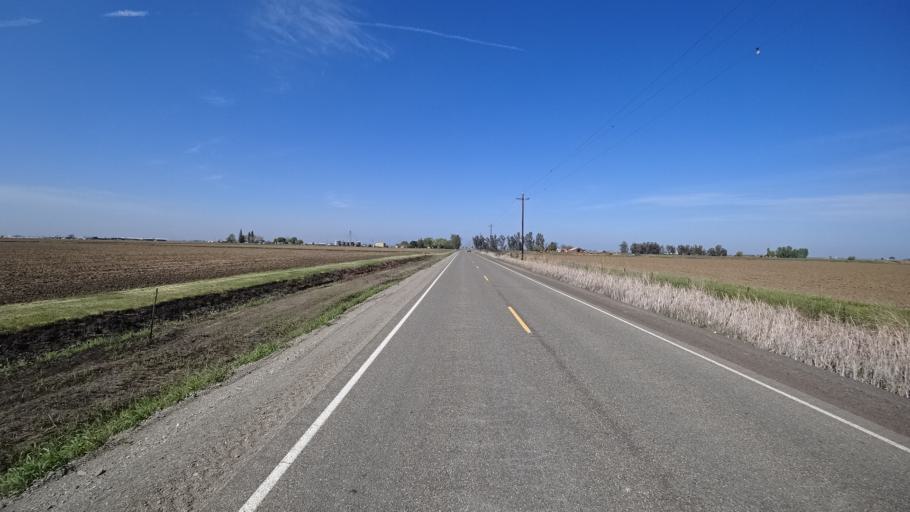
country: US
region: California
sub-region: Glenn County
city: Willows
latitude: 39.5826
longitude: -122.0582
